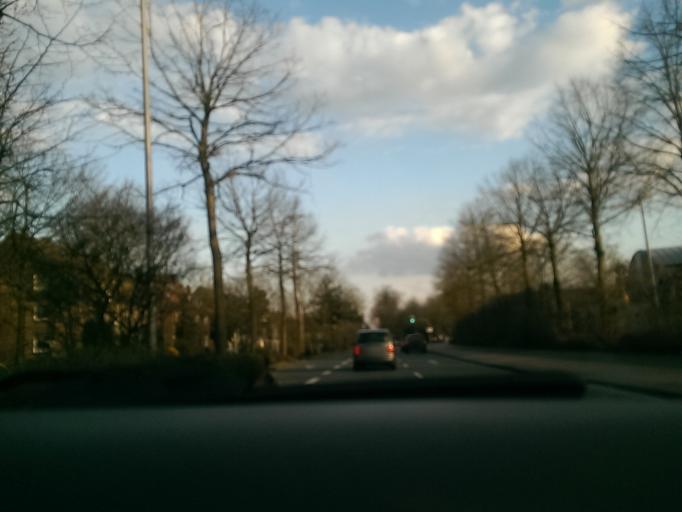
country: DE
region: North Rhine-Westphalia
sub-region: Regierungsbezirk Munster
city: Muenster
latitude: 51.9297
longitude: 7.6662
